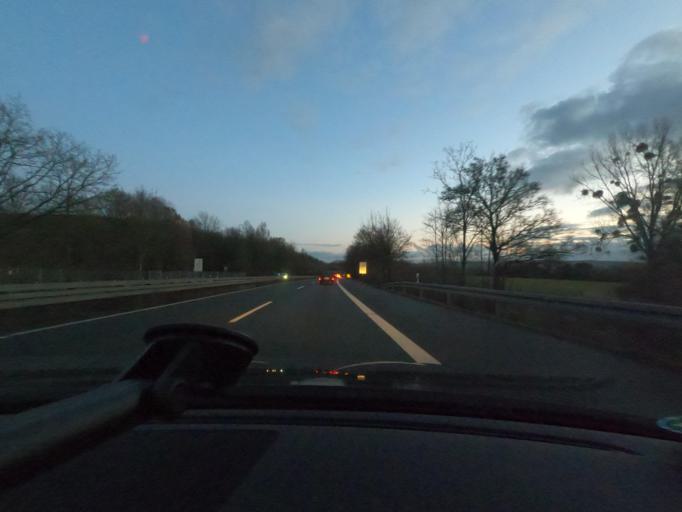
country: DE
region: Lower Saxony
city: Herzberg am Harz
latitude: 51.6387
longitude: 10.3623
